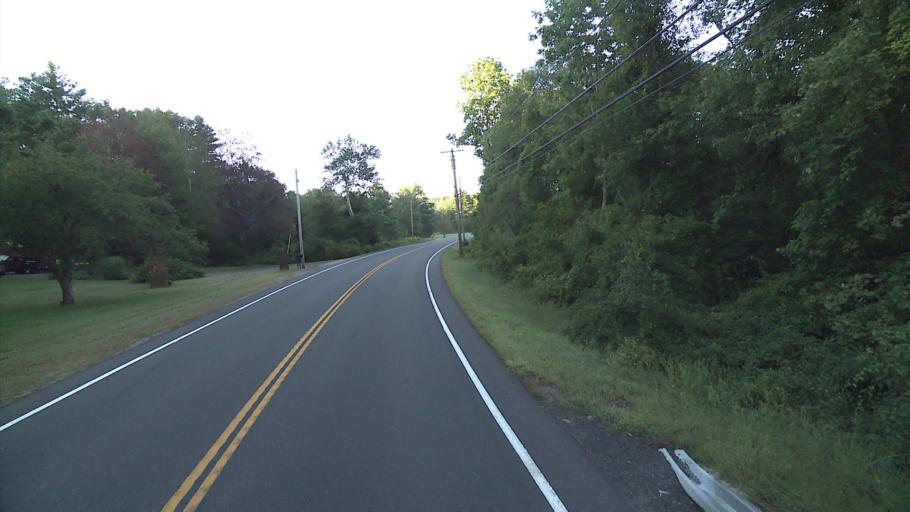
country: US
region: Connecticut
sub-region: Tolland County
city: Stafford
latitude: 42.0130
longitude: -72.3161
